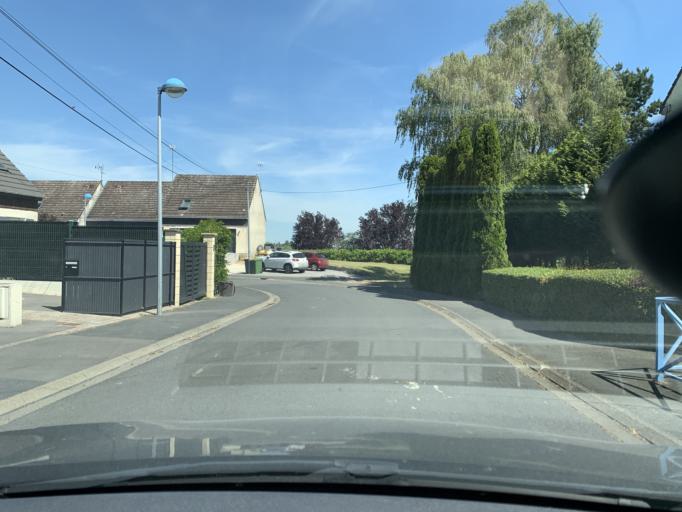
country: FR
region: Nord-Pas-de-Calais
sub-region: Departement du Nord
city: Cambrai
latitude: 50.1571
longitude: 3.2667
